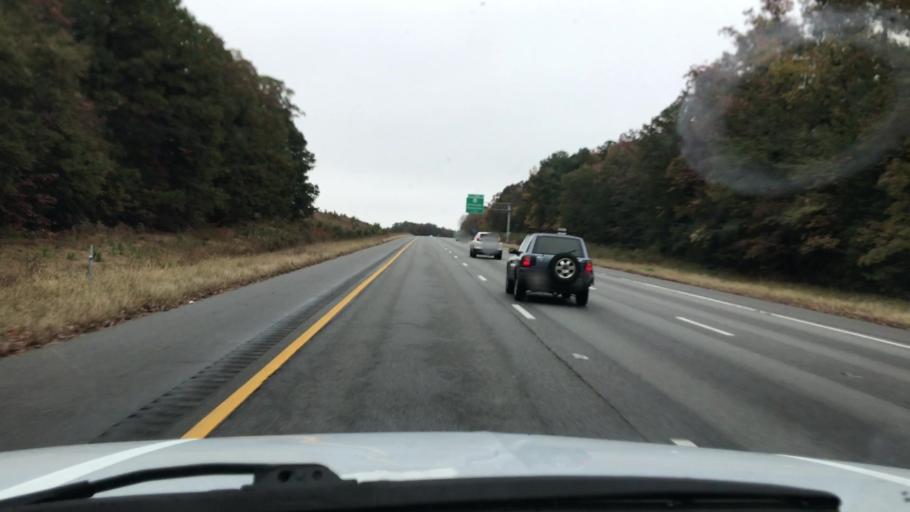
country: US
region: Virginia
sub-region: Henrico County
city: Wyndham
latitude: 37.6751
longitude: -77.5659
